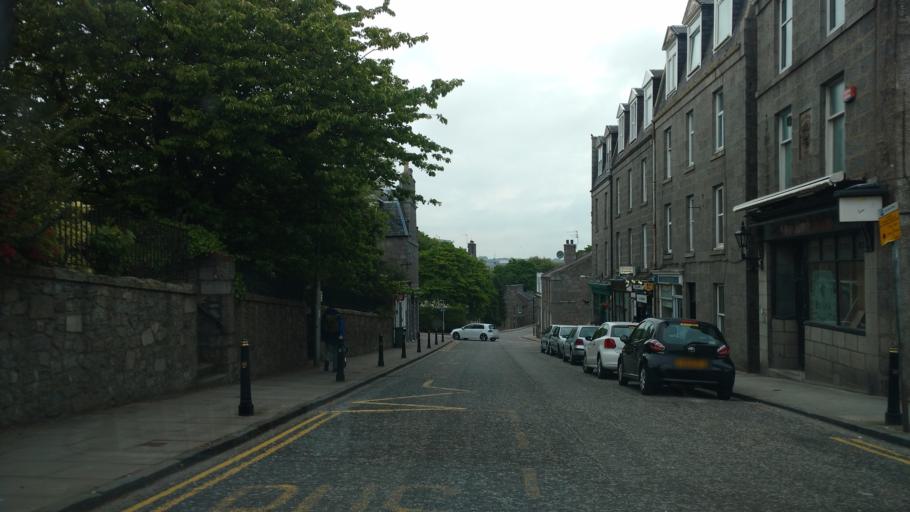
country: GB
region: Scotland
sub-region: Aberdeen City
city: Aberdeen
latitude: 57.1601
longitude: -2.1002
